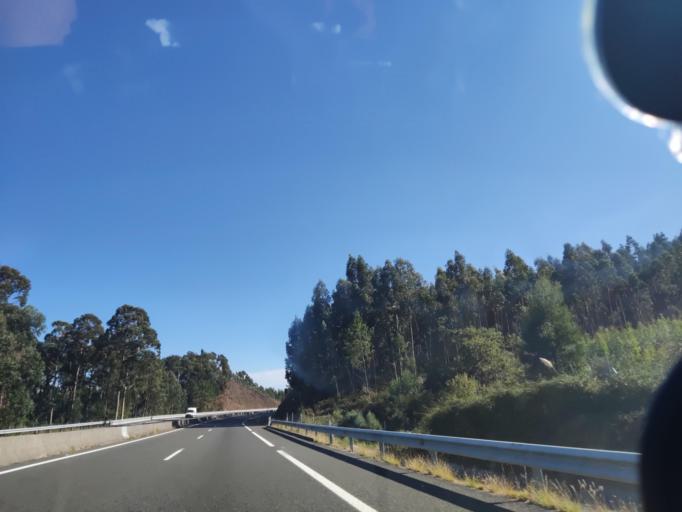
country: ES
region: Galicia
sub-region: Provincia da Coruna
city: Boiro
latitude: 42.5968
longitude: -8.9689
